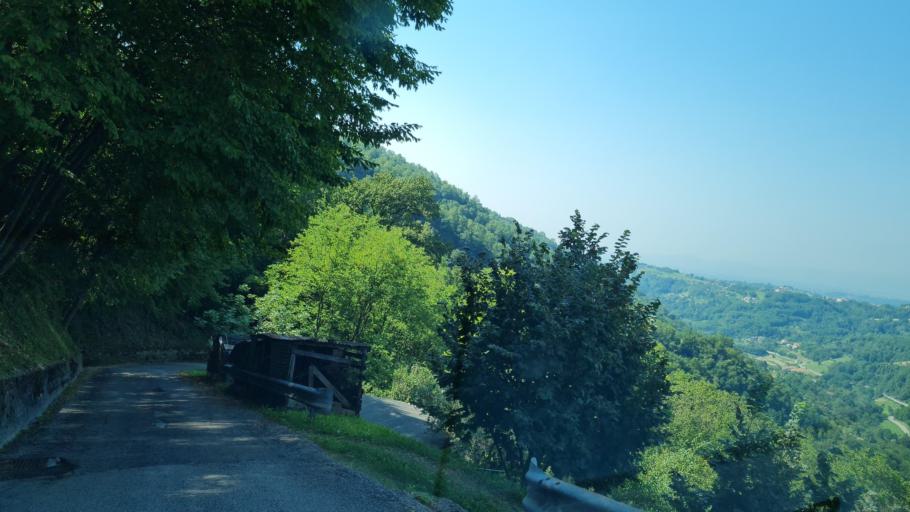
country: IT
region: Veneto
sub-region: Provincia di Vicenza
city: Mure
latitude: 45.7615
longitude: 11.6017
